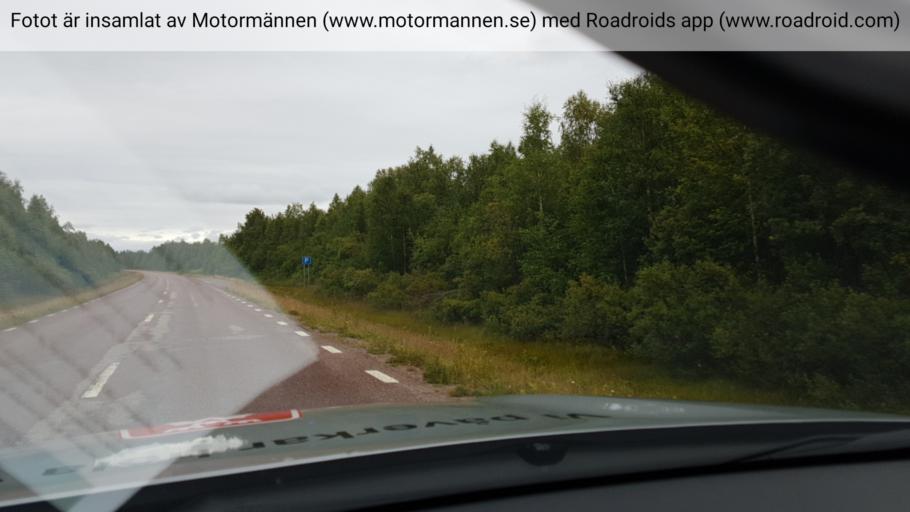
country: SE
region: Norrbotten
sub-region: Pajala Kommun
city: Pajala
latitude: 67.1489
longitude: 22.6257
